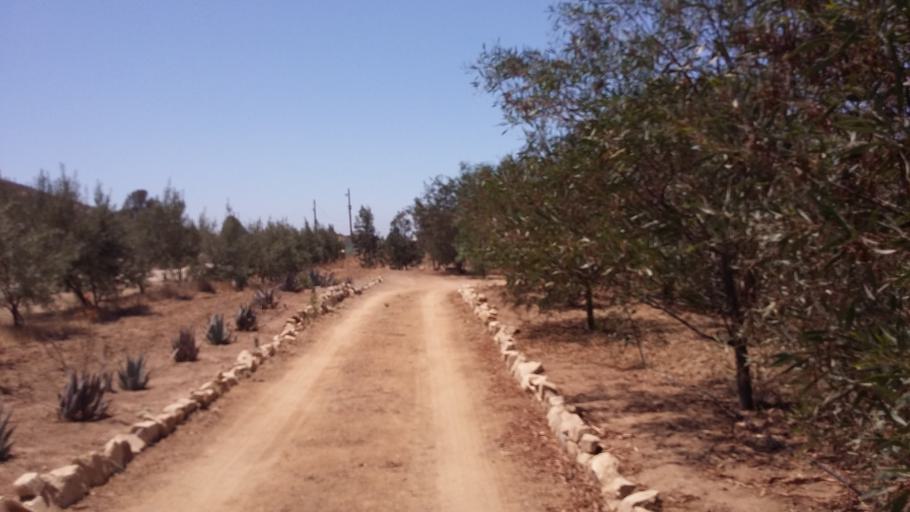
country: MX
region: Baja California
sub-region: Ensenada
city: Rancho Verde
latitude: 32.0326
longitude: -116.6253
